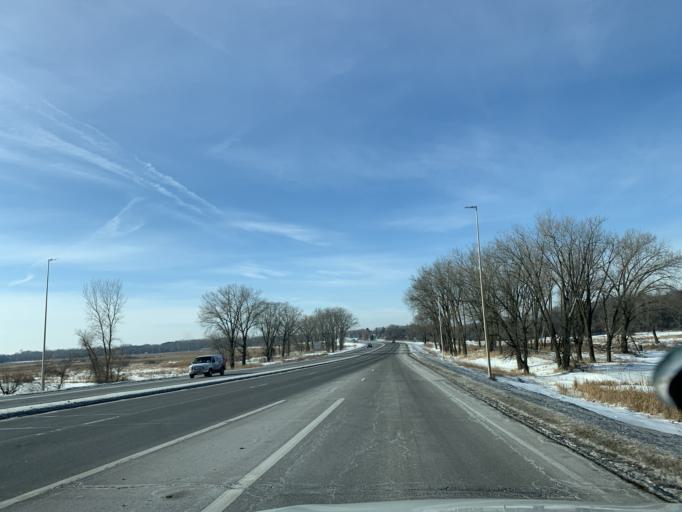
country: US
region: Minnesota
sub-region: Washington County
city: Forest Lake
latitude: 45.2892
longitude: -92.9893
